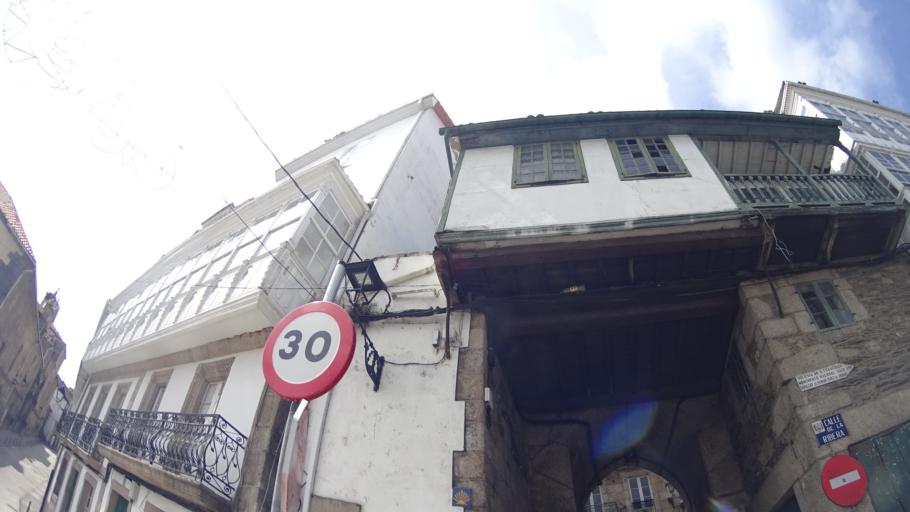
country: ES
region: Galicia
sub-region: Provincia da Coruna
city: Betanzos
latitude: 43.2812
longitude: -8.2094
